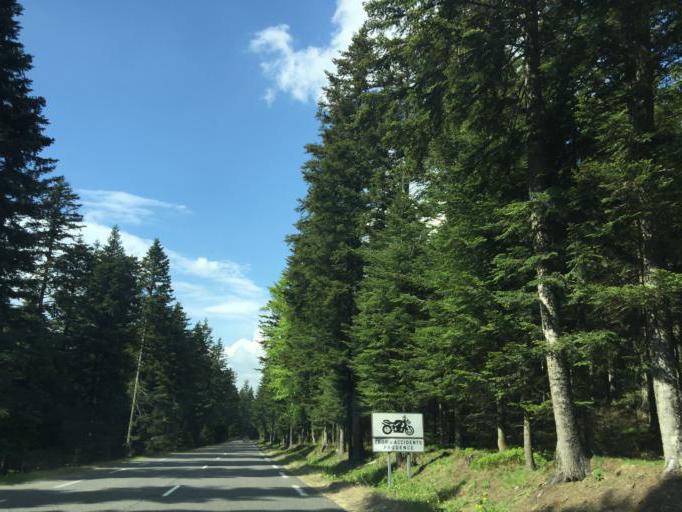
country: FR
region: Rhone-Alpes
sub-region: Departement de la Loire
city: Saint-Genest-Malifaux
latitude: 45.3393
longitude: 4.4788
